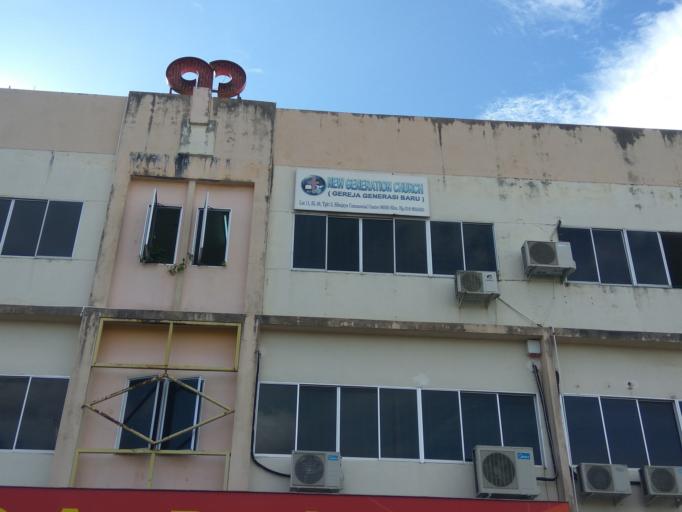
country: MY
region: Sarawak
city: Sibu
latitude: 2.2415
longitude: 111.9759
